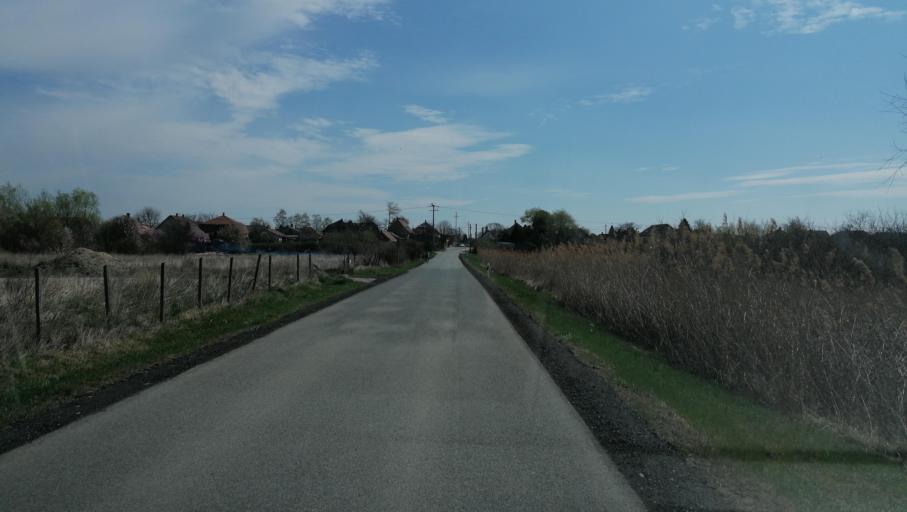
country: HU
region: Pest
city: Kiskunlachaza
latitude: 47.1897
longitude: 18.9991
